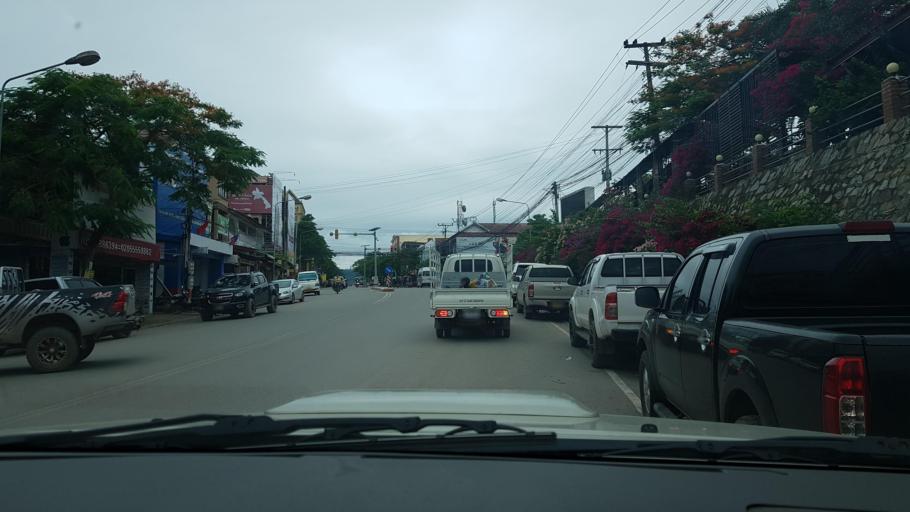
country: LA
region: Oudomxai
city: Muang Xay
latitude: 20.6911
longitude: 101.9832
